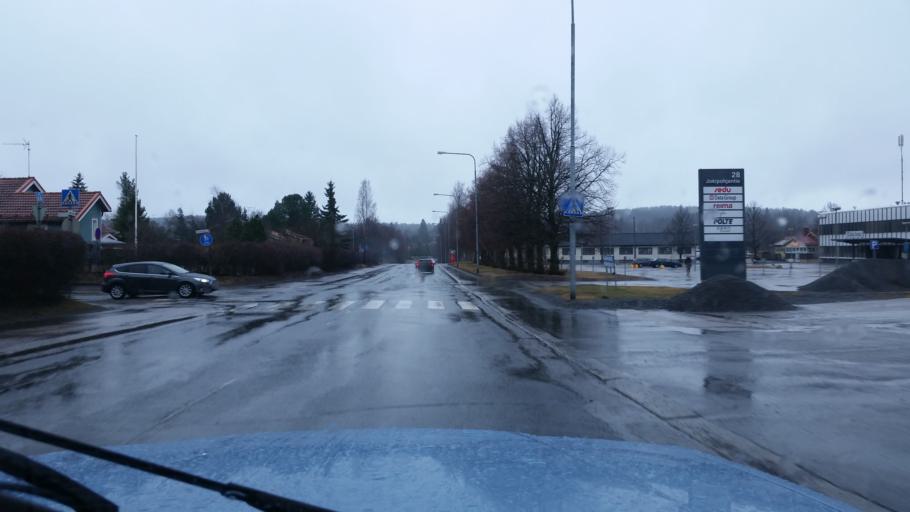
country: FI
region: Pirkanmaa
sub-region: Tampere
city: Tampere
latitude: 61.4775
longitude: 23.7979
